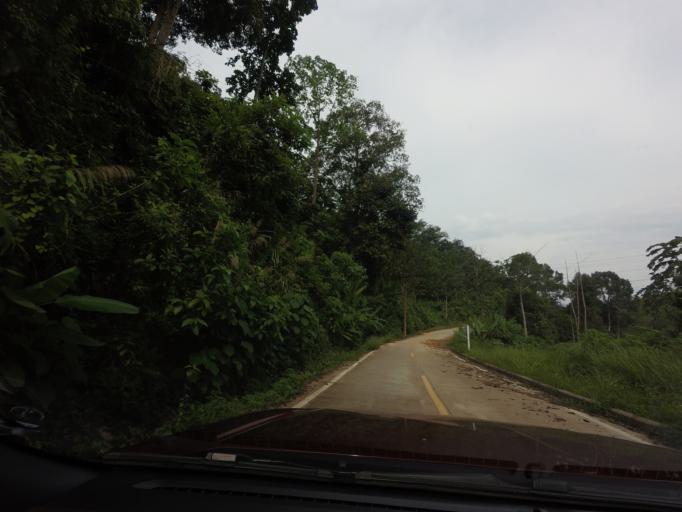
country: TH
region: Yala
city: Than To
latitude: 6.0673
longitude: 101.3574
